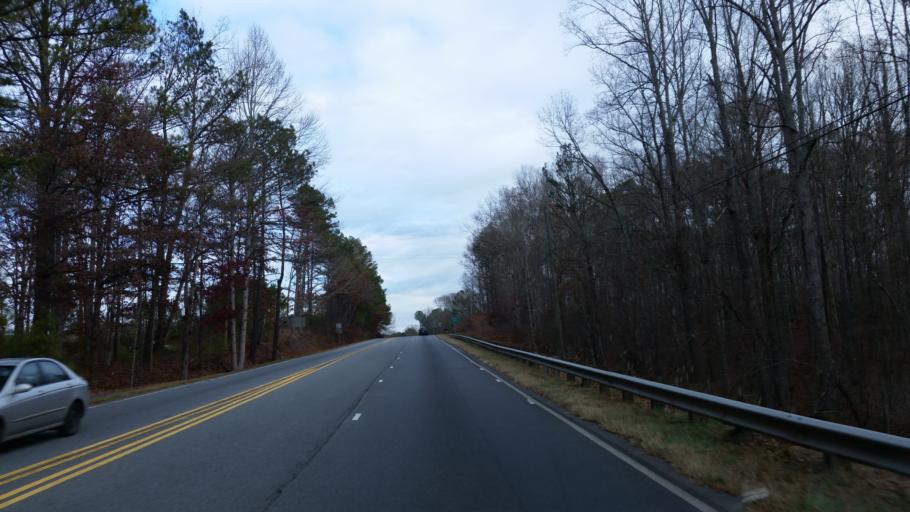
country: US
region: Georgia
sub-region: Bartow County
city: Emerson
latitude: 34.2138
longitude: -84.6548
